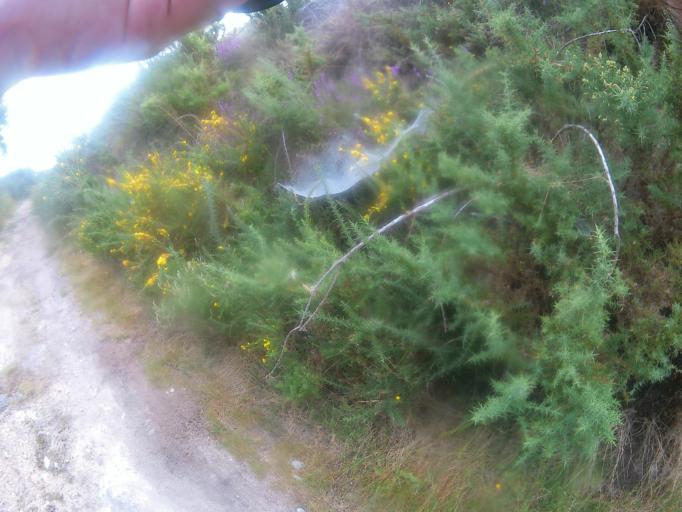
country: PT
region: Viana do Castelo
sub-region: Ponte de Lima
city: Ponte de Lima
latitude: 41.7177
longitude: -8.6031
